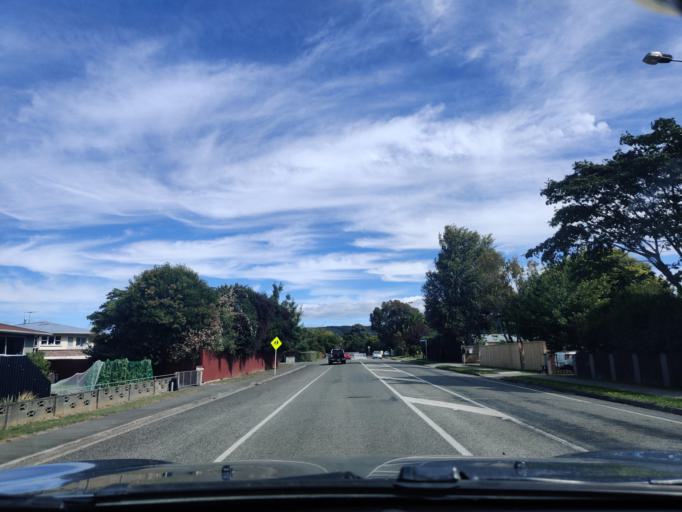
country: NZ
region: Tasman
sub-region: Tasman District
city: Wakefield
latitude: -41.4045
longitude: 173.0494
